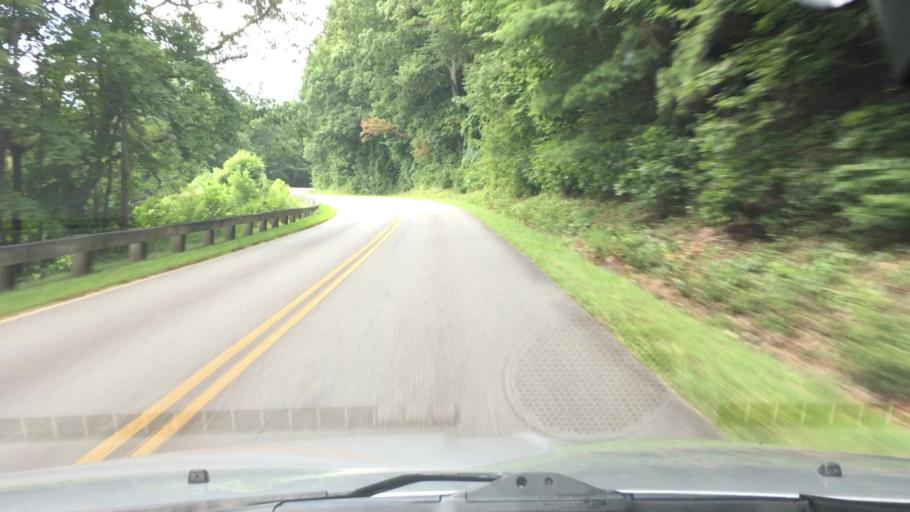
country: US
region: North Carolina
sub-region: Buncombe County
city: Asheville
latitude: 35.6194
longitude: -82.4926
